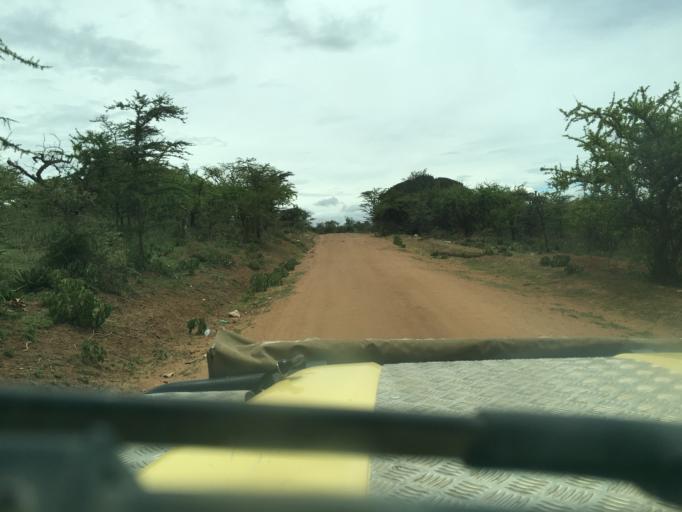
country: KE
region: Kajiado
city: Magadi
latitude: -2.0189
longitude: 35.5275
